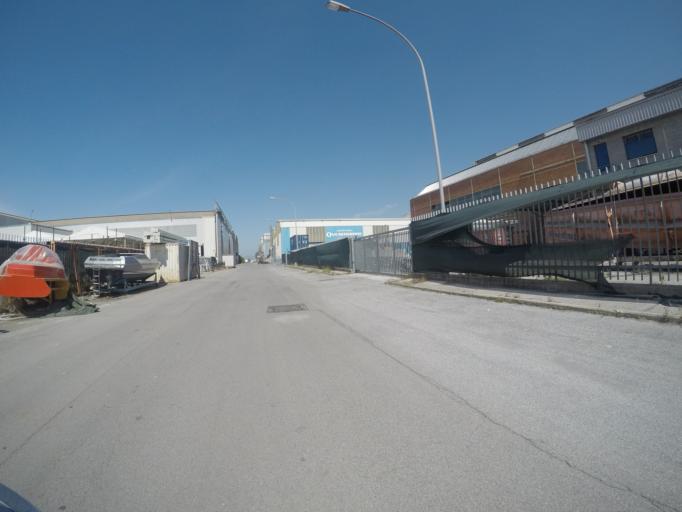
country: IT
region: Tuscany
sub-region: Provincia di Massa-Carrara
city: Massa
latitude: 44.0266
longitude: 10.1026
